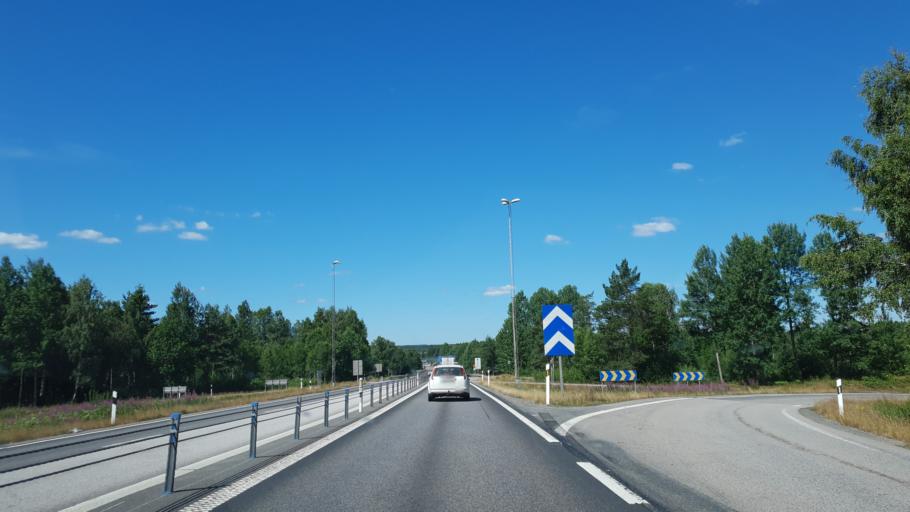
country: SE
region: Kronoberg
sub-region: Alvesta Kommun
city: Alvesta
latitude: 56.9214
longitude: 14.5712
